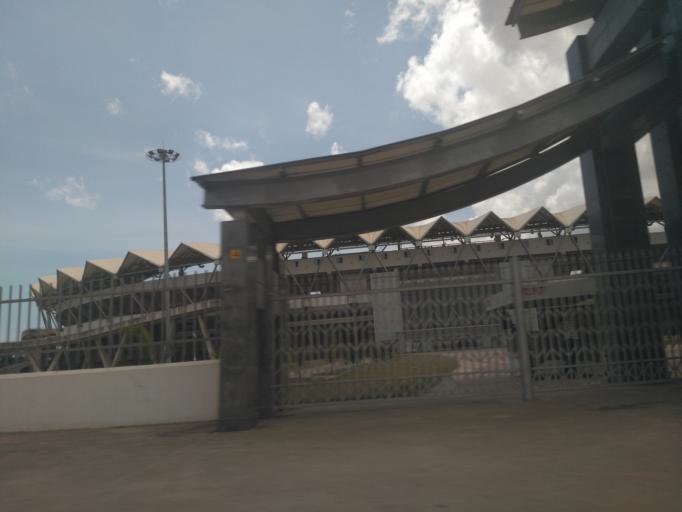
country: TZ
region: Dar es Salaam
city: Dar es Salaam
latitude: -6.8534
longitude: 39.2717
